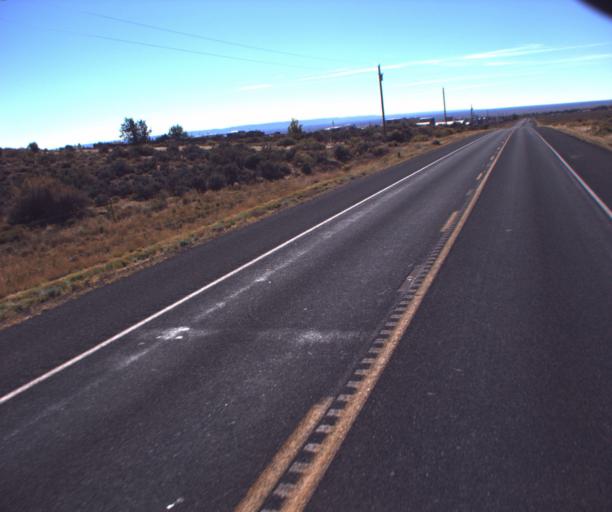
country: US
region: Arizona
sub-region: Coconino County
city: Fredonia
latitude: 36.9791
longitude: -112.5289
